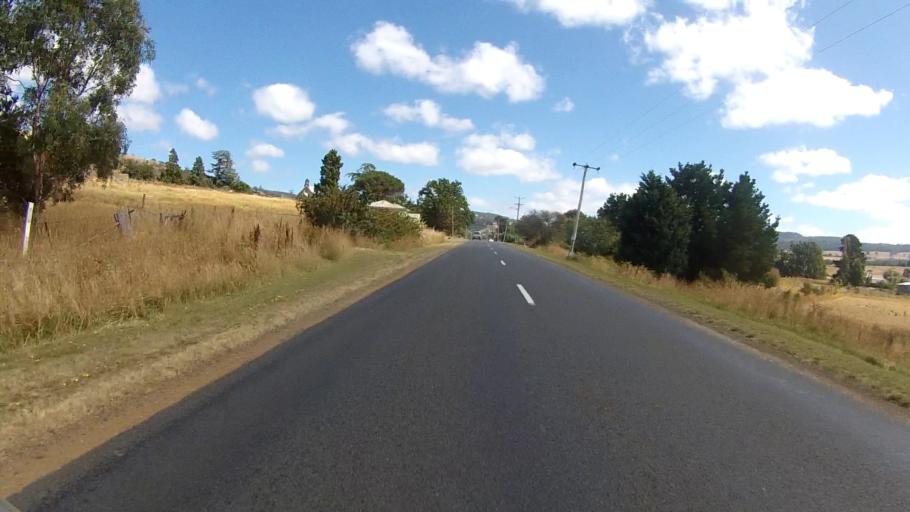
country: AU
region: Tasmania
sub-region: Brighton
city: Bridgewater
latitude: -42.5376
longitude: 147.3670
